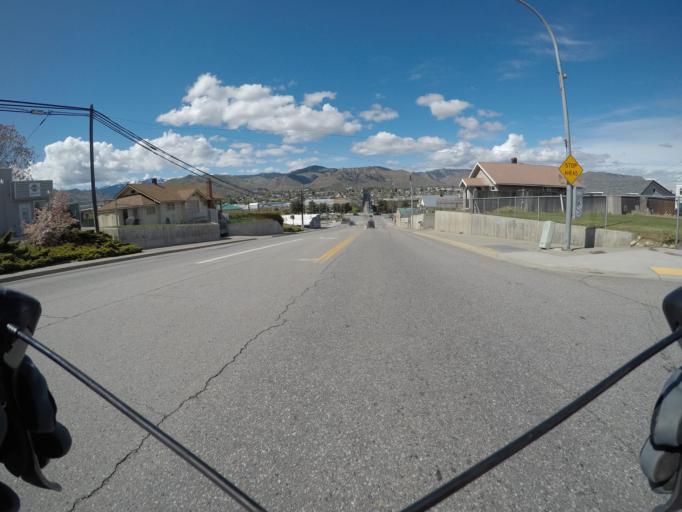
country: US
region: Washington
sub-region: Douglas County
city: East Wenatchee
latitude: 47.4161
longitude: -120.2921
